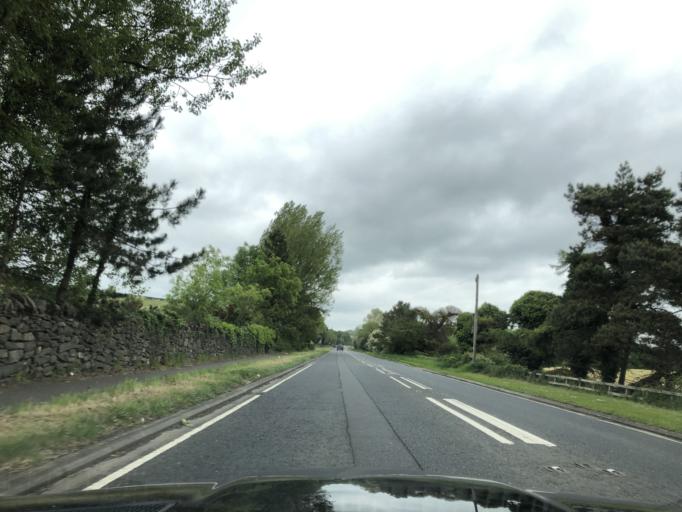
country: GB
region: Northern Ireland
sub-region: Down District
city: Downpatrick
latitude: 54.3494
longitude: -5.7360
